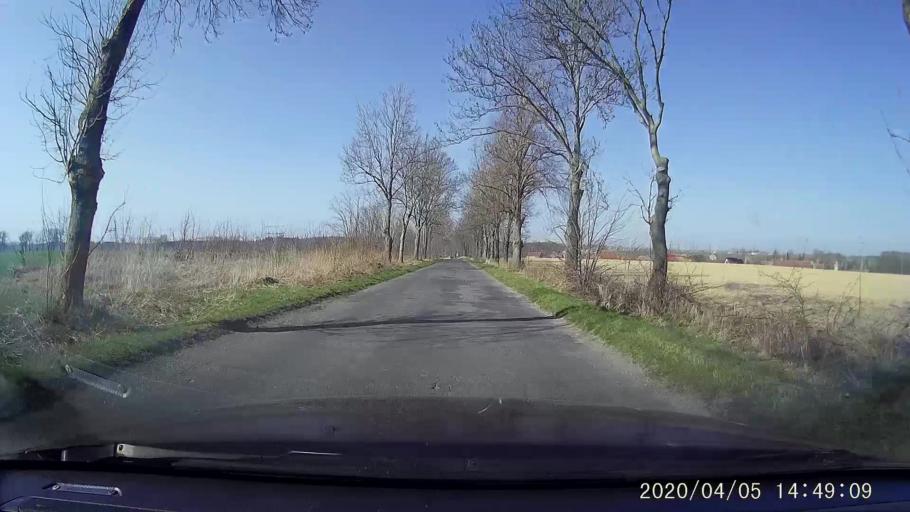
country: PL
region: Lower Silesian Voivodeship
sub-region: Powiat zgorzelecki
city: Sulikow
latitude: 51.0755
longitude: 15.1038
